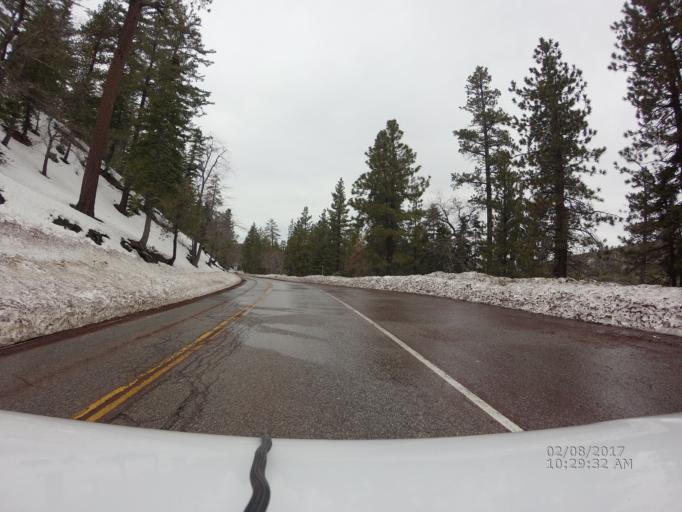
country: US
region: California
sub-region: San Bernardino County
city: Pinon Hills
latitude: 34.3880
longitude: -117.7149
